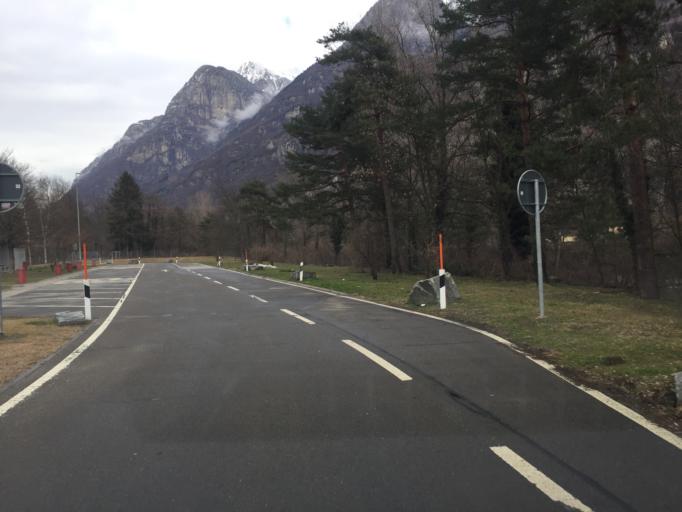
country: CH
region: Ticino
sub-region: Riviera District
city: Lodrino
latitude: 46.2794
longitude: 8.9964
